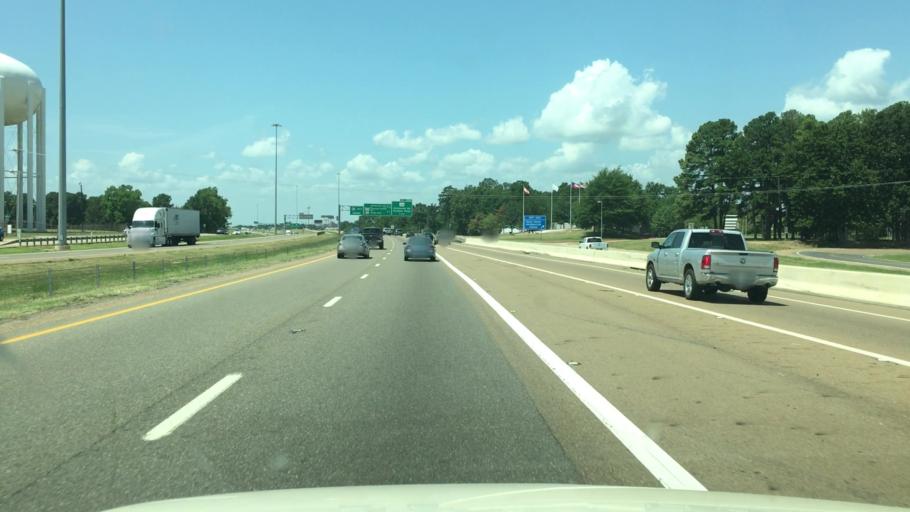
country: US
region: Arkansas
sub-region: Miller County
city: Texarkana
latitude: 33.4701
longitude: -94.0522
